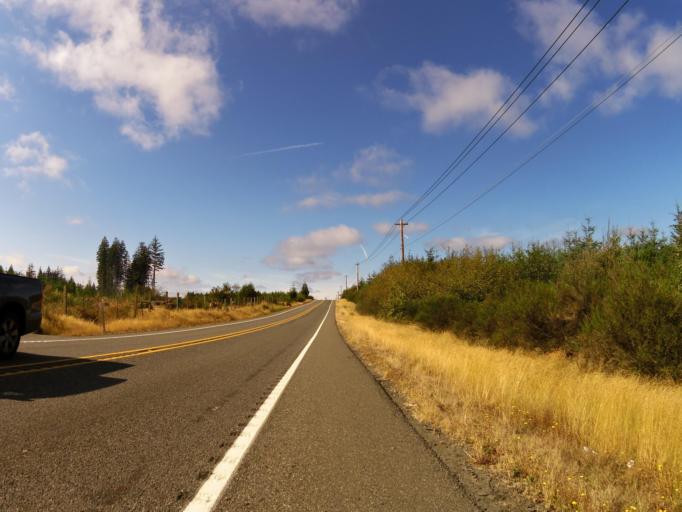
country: US
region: Washington
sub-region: Mason County
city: Allyn
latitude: 47.3274
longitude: -122.8897
